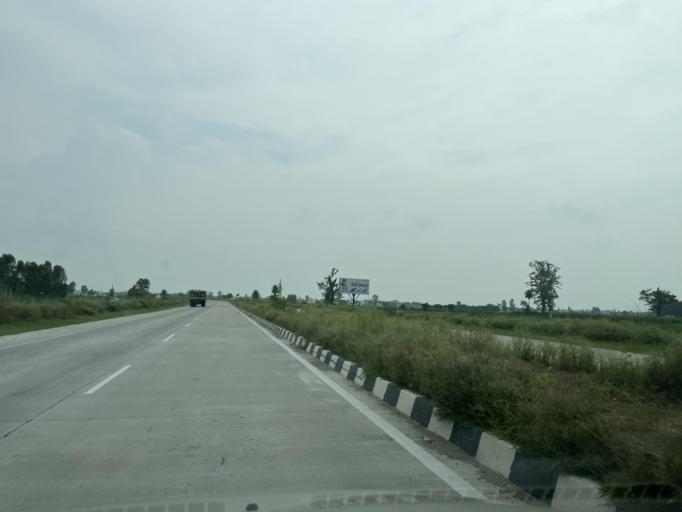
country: IN
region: Uttarakhand
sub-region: Udham Singh Nagar
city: Kashipur
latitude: 29.1821
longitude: 78.9395
